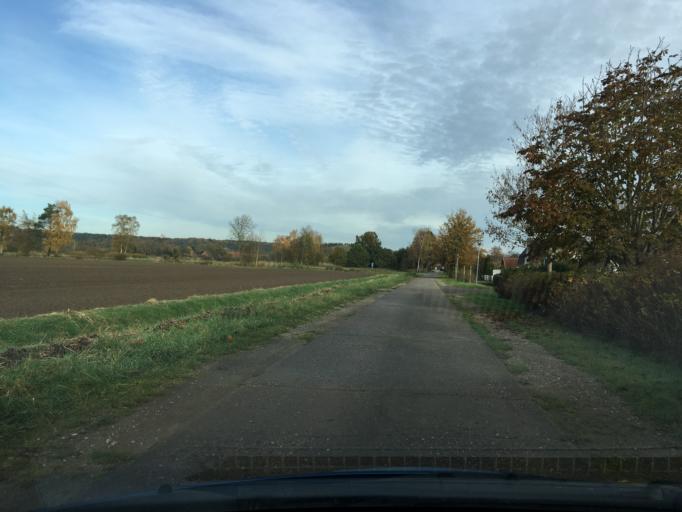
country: DE
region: Lower Saxony
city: Artlenburg
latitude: 53.3691
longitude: 10.4764
